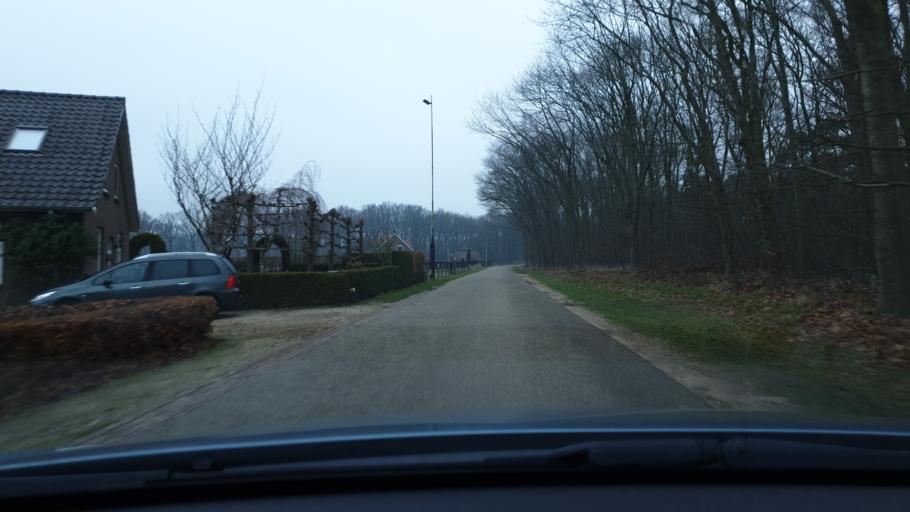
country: NL
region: Gelderland
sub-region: Gemeente Wijchen
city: Bergharen
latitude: 51.8580
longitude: 5.6682
